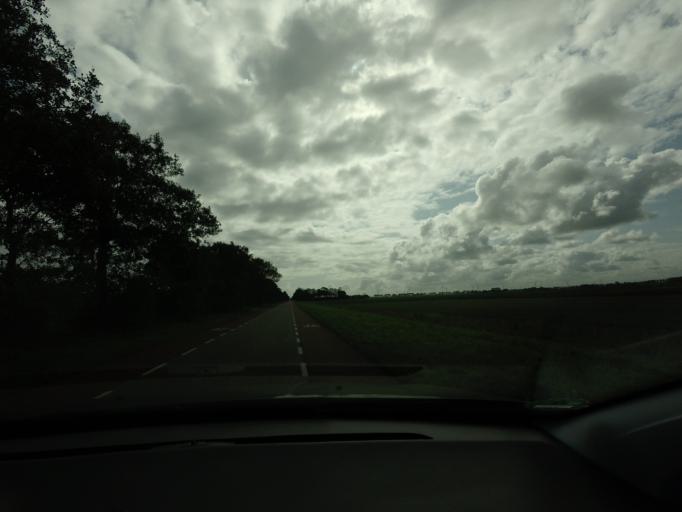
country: NL
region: North Holland
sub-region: Gemeente Hollands Kroon
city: Den Oever
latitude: 52.8719
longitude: 5.0907
